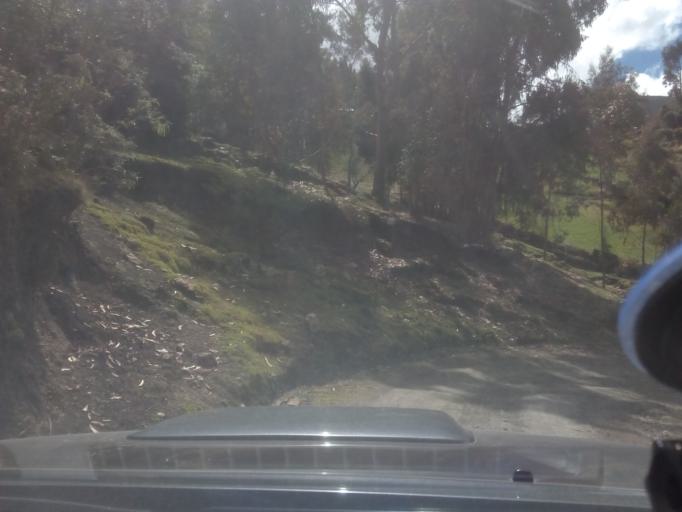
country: PE
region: Ayacucho
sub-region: Provincia de Huanta
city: Luricocha
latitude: -12.8790
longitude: -74.2240
